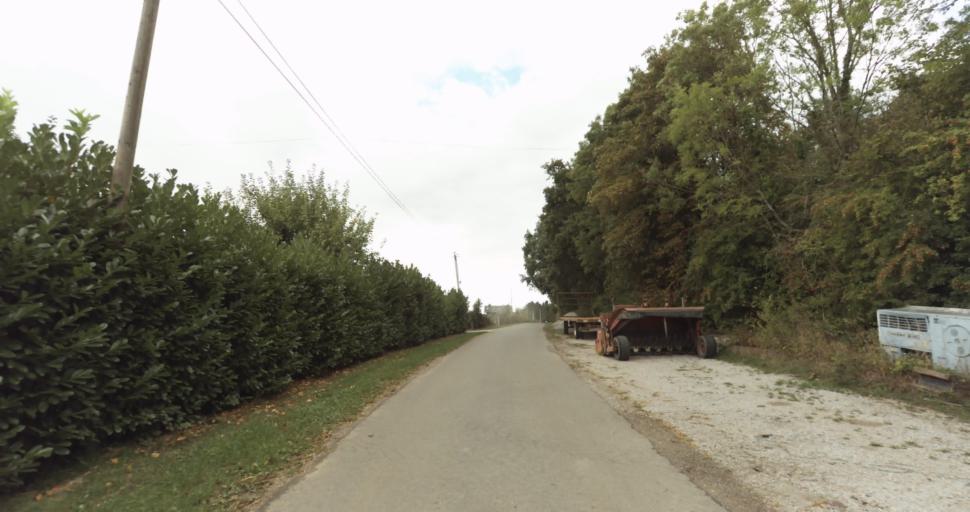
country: FR
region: Lower Normandy
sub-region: Departement de l'Orne
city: Sainte-Gauburge-Sainte-Colombe
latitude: 48.7267
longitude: 0.3960
